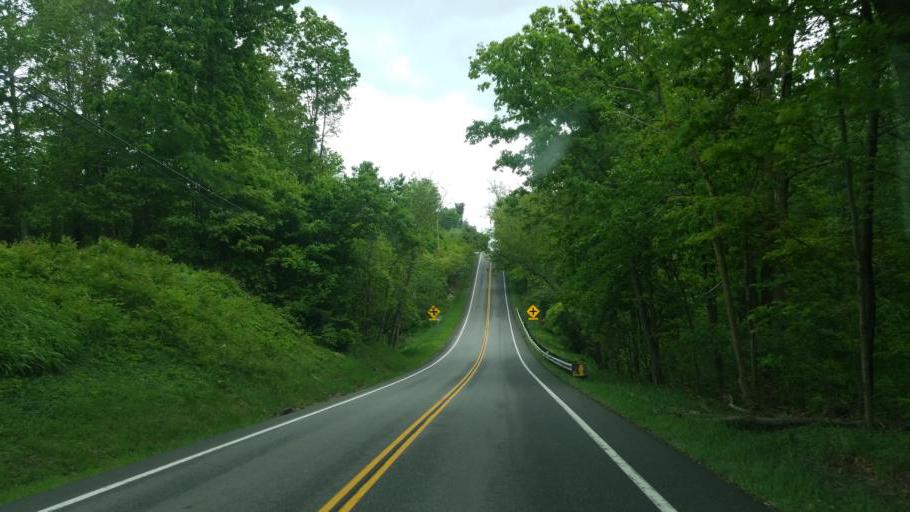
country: US
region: Ohio
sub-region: Summit County
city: Richfield
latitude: 41.2397
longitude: -81.7057
